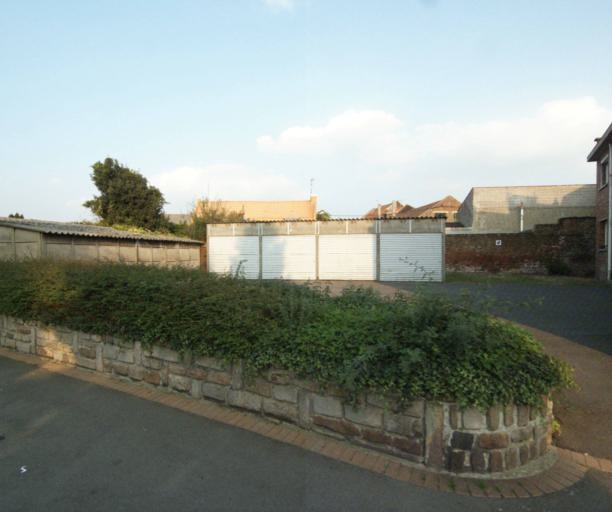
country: FR
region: Nord-Pas-de-Calais
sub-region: Departement du Nord
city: Emmerin
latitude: 50.5923
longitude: 2.9967
